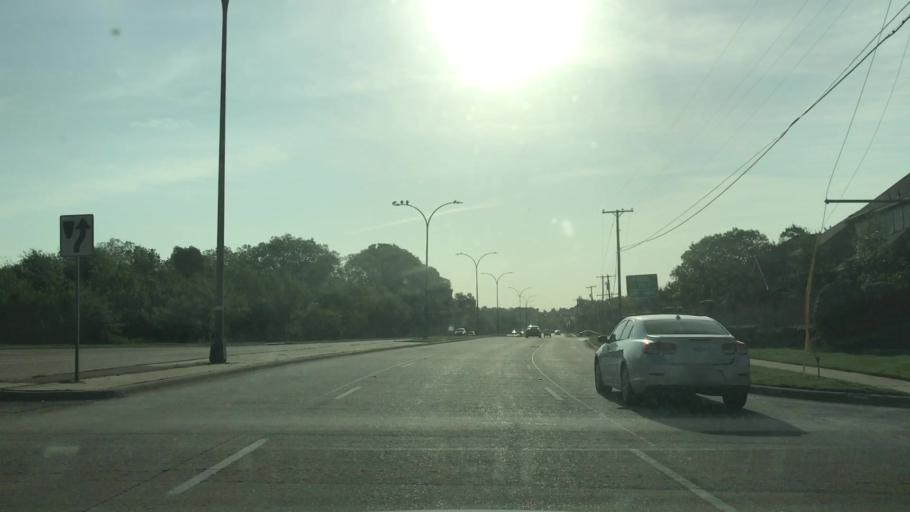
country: US
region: Texas
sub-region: Tarrant County
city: Arlington
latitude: 32.7793
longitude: -97.1336
